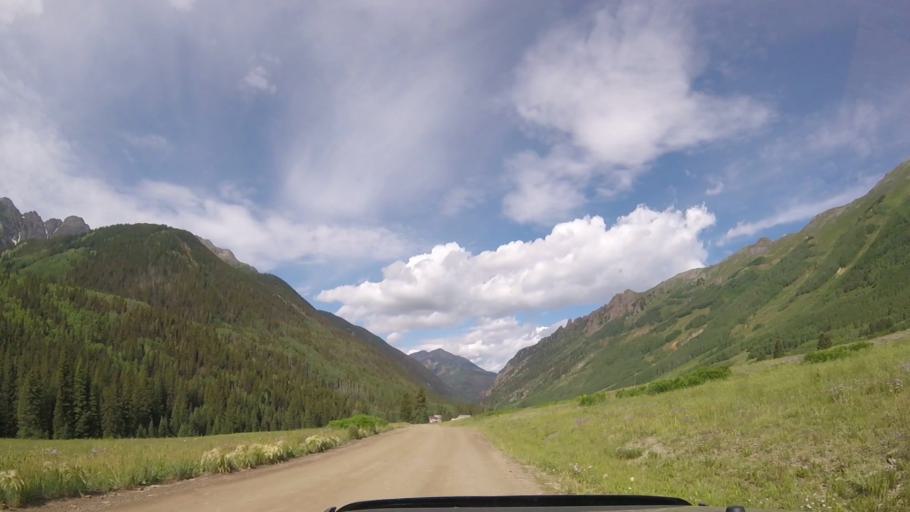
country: US
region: Colorado
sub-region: San Miguel County
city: Mountain Village
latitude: 37.8557
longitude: -107.8280
